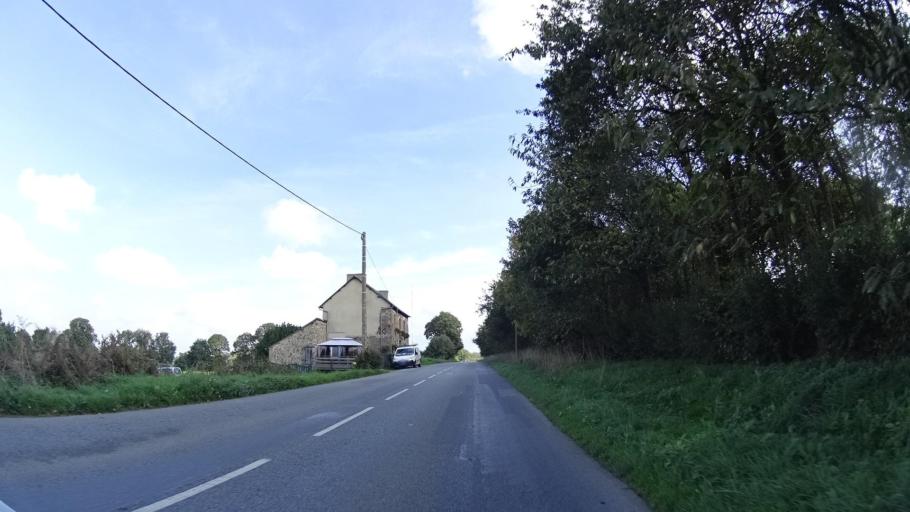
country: FR
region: Brittany
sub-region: Departement des Cotes-d'Armor
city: Plouasne
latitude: 48.2850
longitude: -1.9804
